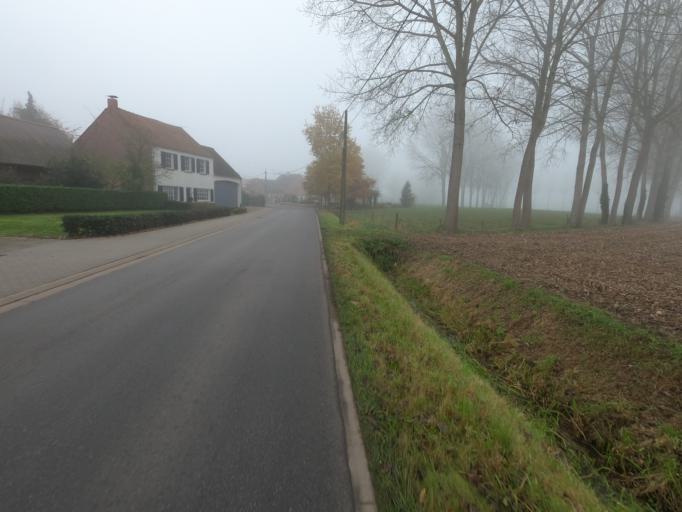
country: BE
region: Flanders
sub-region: Provincie Oost-Vlaanderen
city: Kruibeke
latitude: 51.1766
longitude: 4.2908
